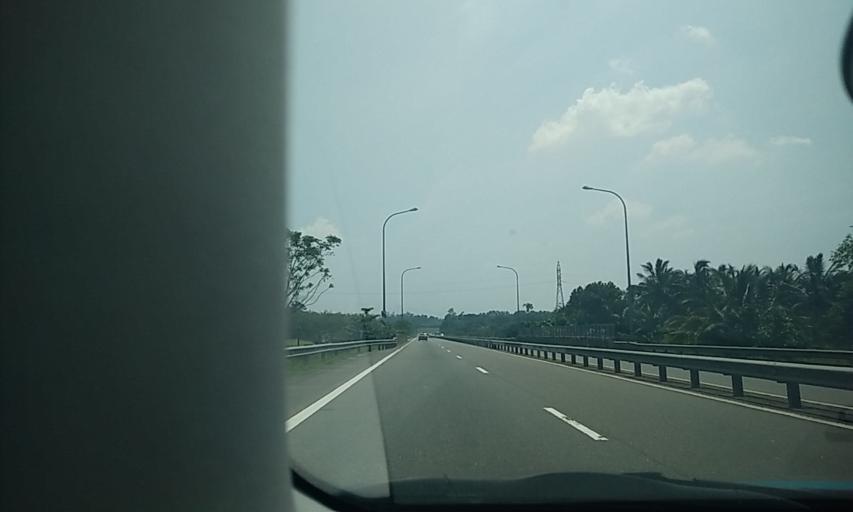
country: LK
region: Western
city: Horana South
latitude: 6.7580
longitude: 79.9910
